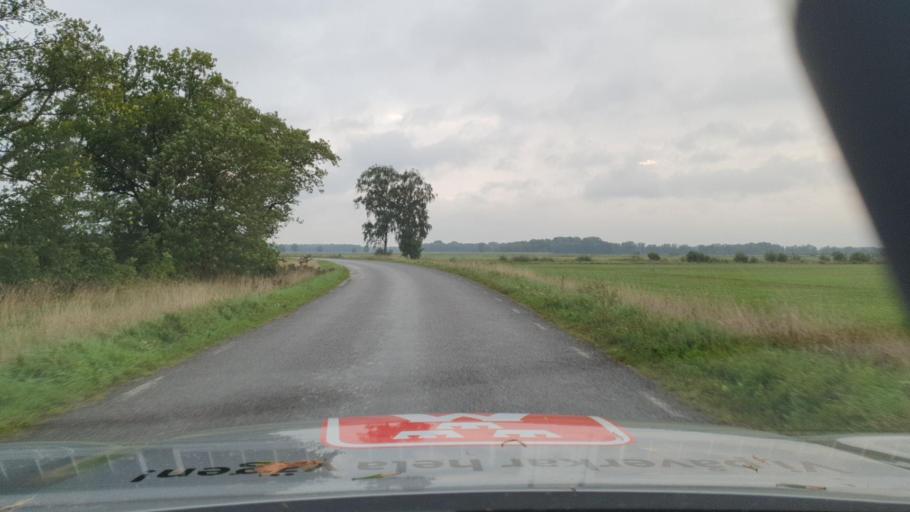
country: SE
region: Gotland
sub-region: Gotland
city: Visby
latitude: 57.4880
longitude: 18.4609
